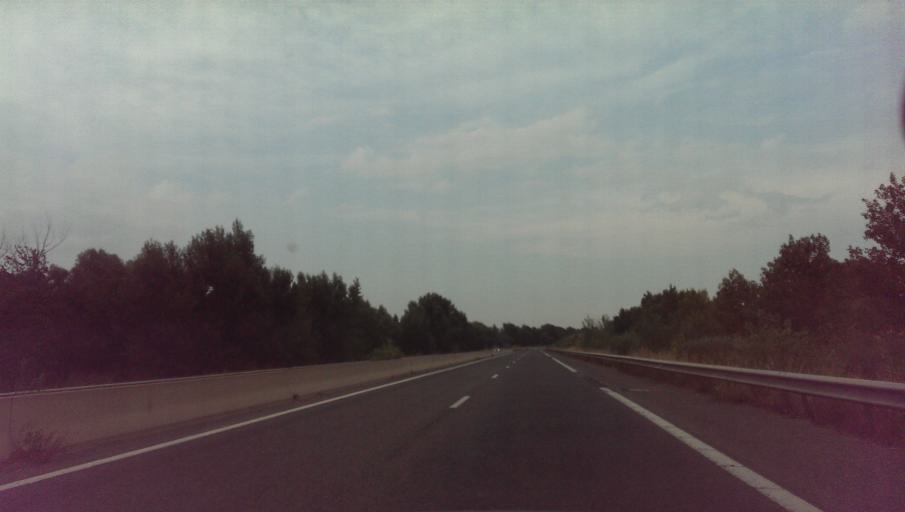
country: FR
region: Languedoc-Roussillon
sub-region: Departement des Pyrenees-Orientales
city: Pezilla-la-Riviere
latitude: 42.6833
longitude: 2.7605
